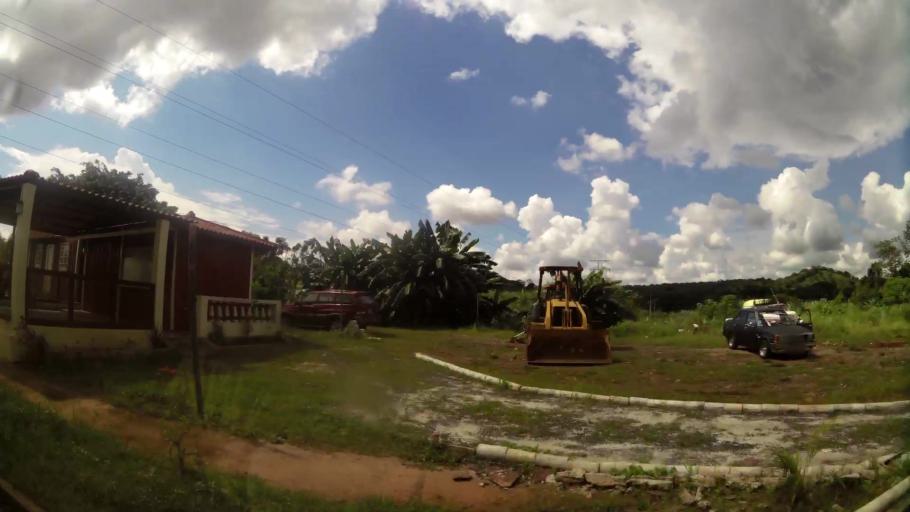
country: PA
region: Panama
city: Nuevo Arraijan
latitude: 8.9338
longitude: -79.7368
